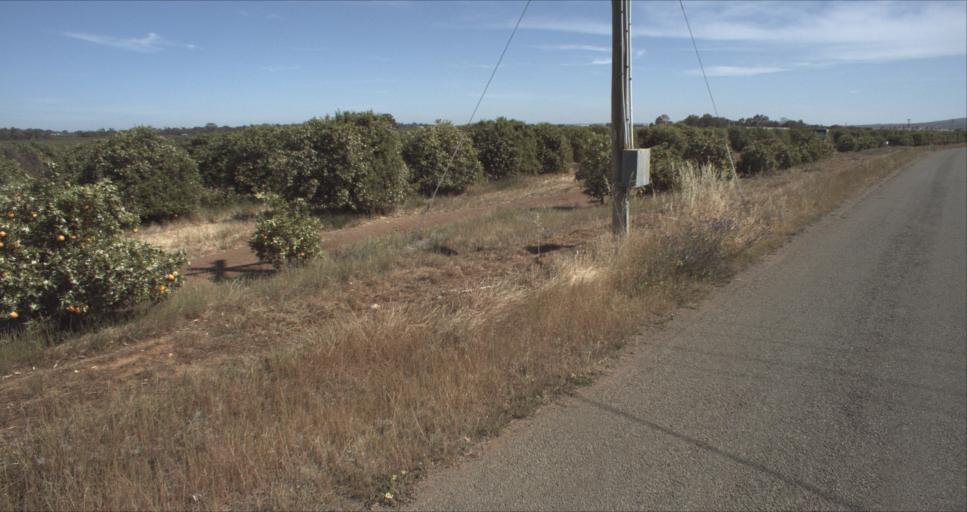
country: AU
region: New South Wales
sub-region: Leeton
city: Leeton
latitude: -34.5811
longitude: 146.4772
